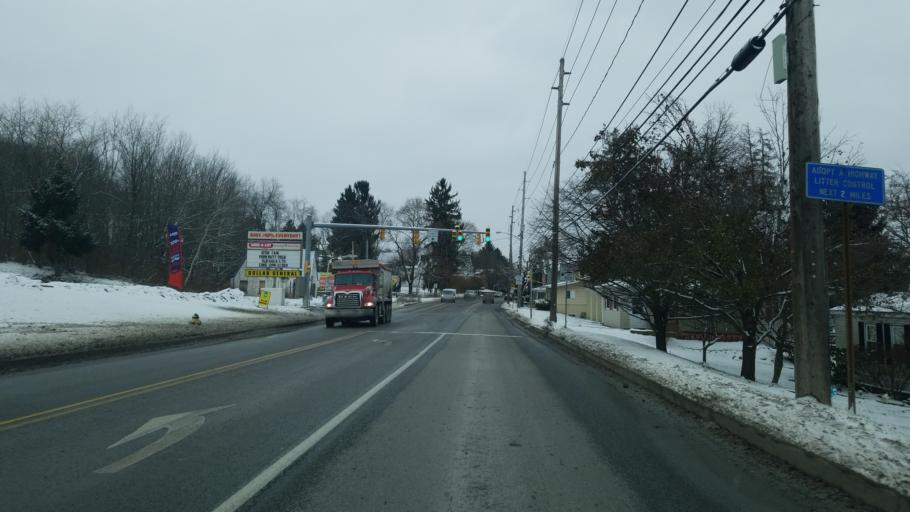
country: US
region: Pennsylvania
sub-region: Clearfield County
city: Sandy
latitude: 41.1047
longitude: -78.7709
